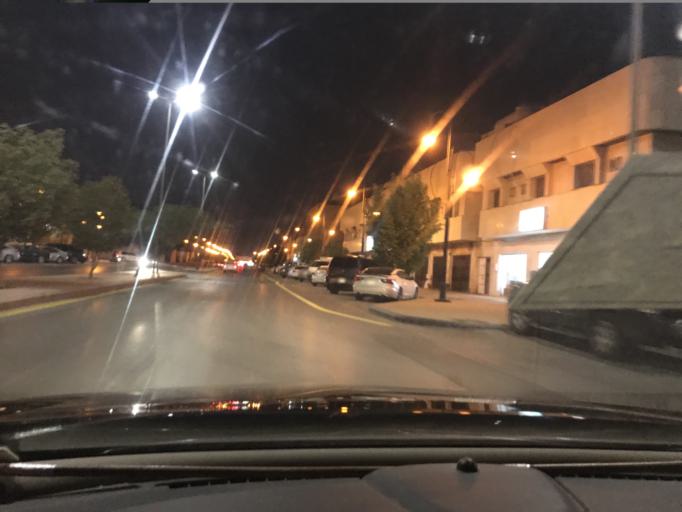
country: SA
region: Ar Riyad
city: Riyadh
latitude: 24.7409
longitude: 46.7703
